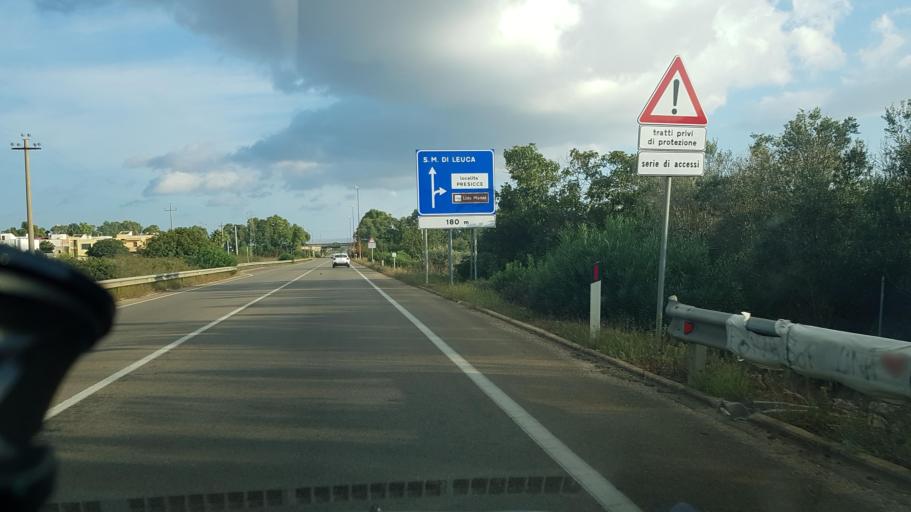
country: IT
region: Apulia
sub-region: Provincia di Lecce
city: Presicce
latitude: 39.8978
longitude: 18.2534
